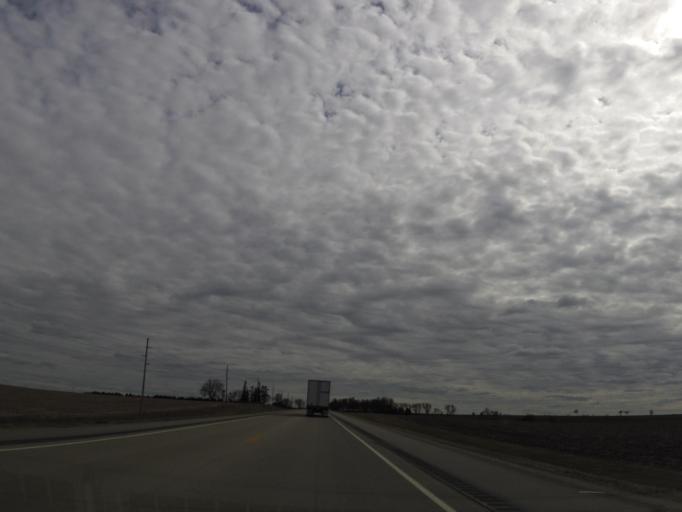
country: US
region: Minnesota
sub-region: Fillmore County
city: Spring Valley
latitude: 43.5979
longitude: -92.3893
